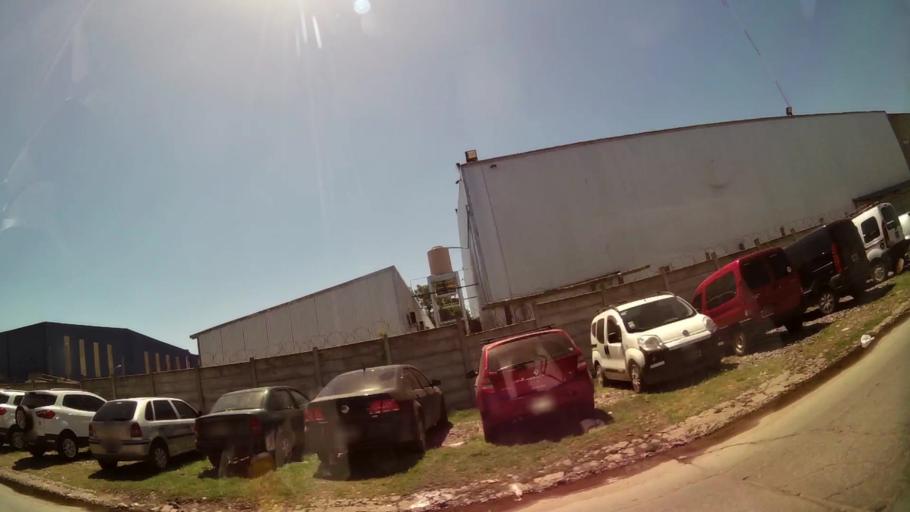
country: AR
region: Buenos Aires
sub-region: Partido de Tigre
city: Tigre
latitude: -34.4820
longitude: -58.6486
